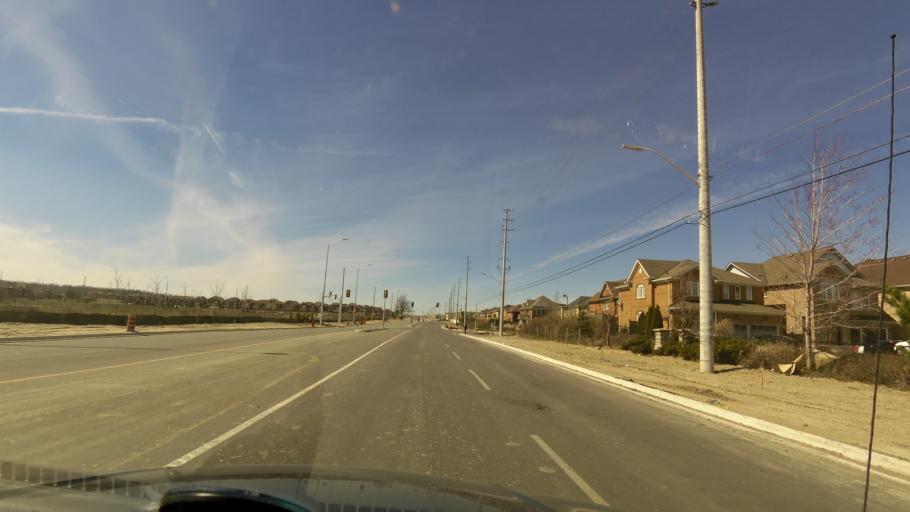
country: CA
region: Ontario
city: Brampton
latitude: 43.6943
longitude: -79.8430
